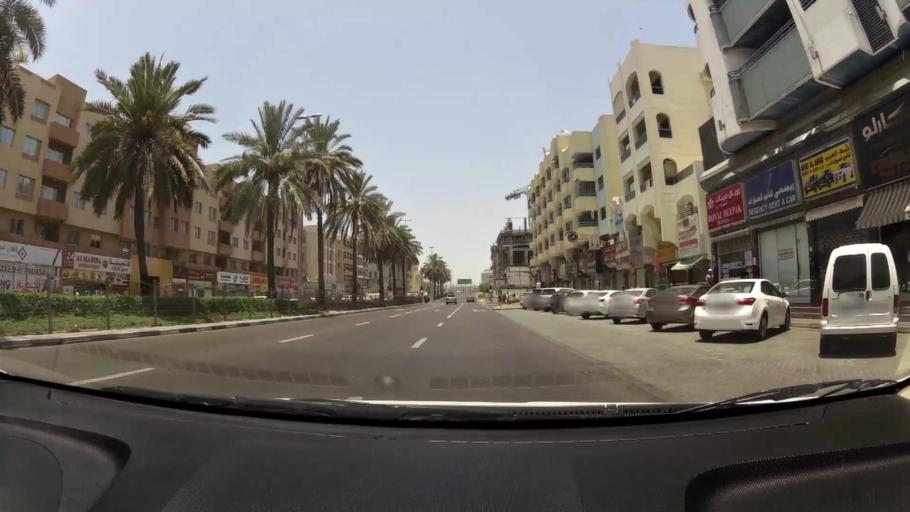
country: AE
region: Ash Shariqah
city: Sharjah
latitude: 25.2722
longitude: 55.3162
